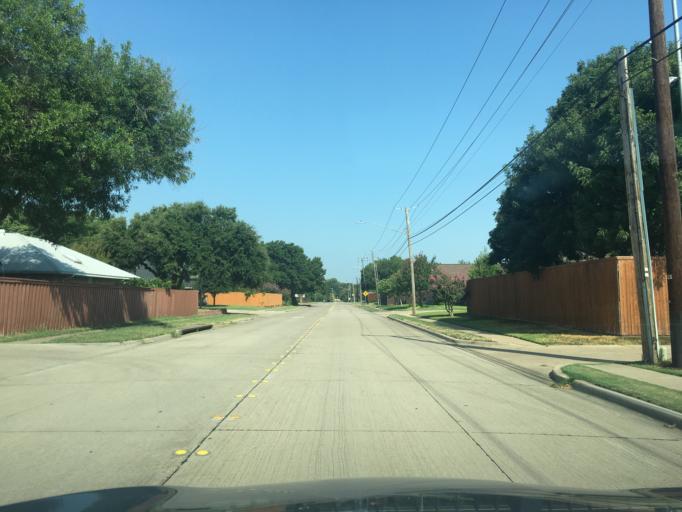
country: US
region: Texas
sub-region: Dallas County
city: Garland
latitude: 32.9430
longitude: -96.6345
